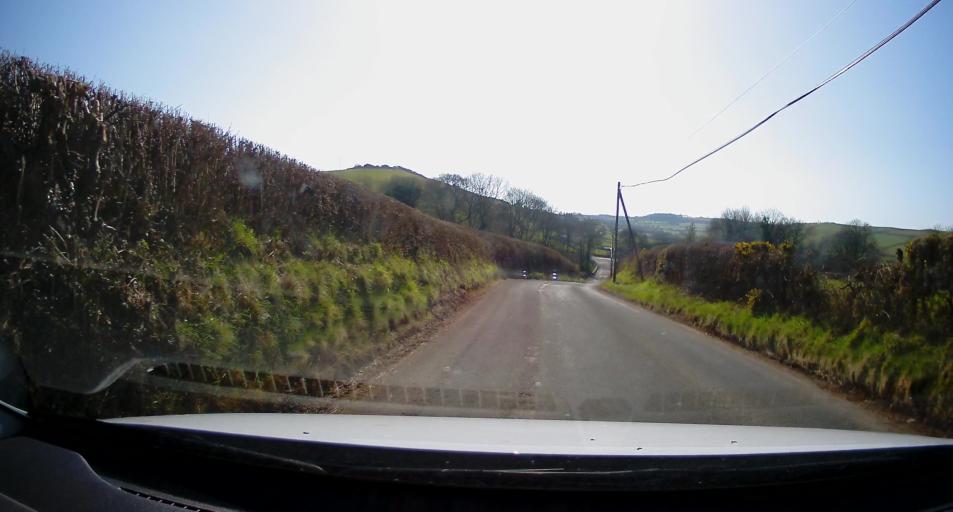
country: GB
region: Wales
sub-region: County of Ceredigion
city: Penparcau
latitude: 52.3493
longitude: -4.0639
